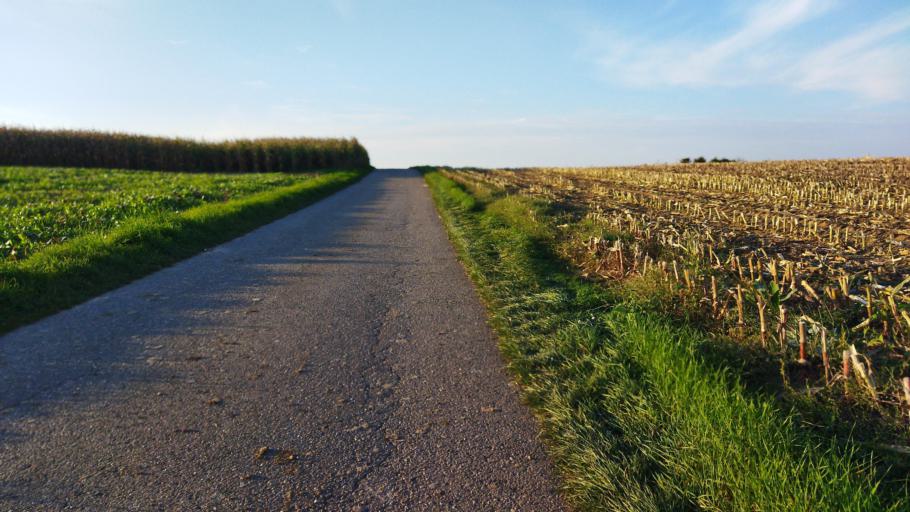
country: DE
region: Baden-Wuerttemberg
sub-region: Regierungsbezirk Stuttgart
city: Abstatt
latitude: 49.0453
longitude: 9.2754
